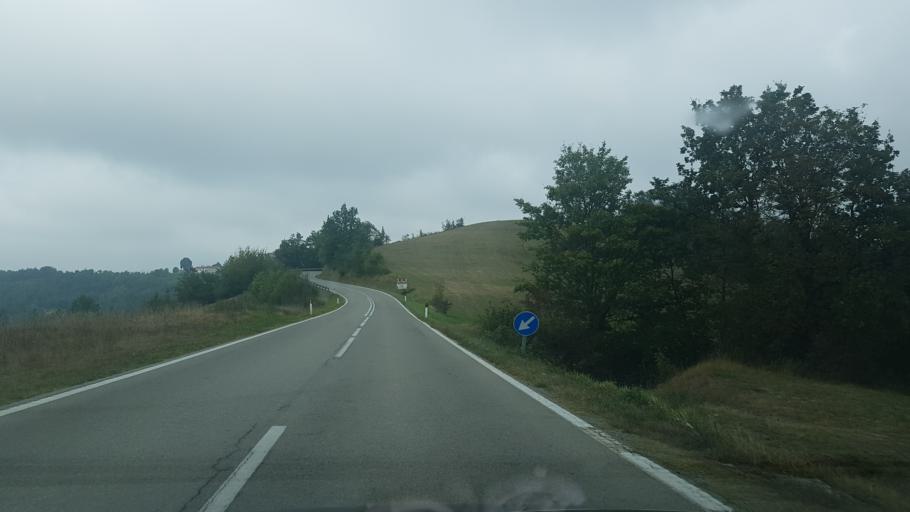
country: IT
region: Piedmont
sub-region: Provincia di Cuneo
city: Sale San Giovanni
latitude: 44.4108
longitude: 8.0944
